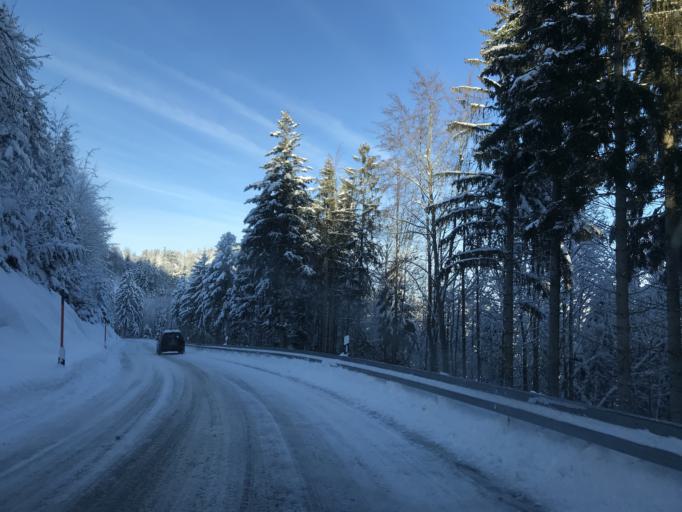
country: DE
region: Baden-Wuerttemberg
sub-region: Freiburg Region
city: Muenstertal/Schwarzwald
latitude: 47.8096
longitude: 7.7809
